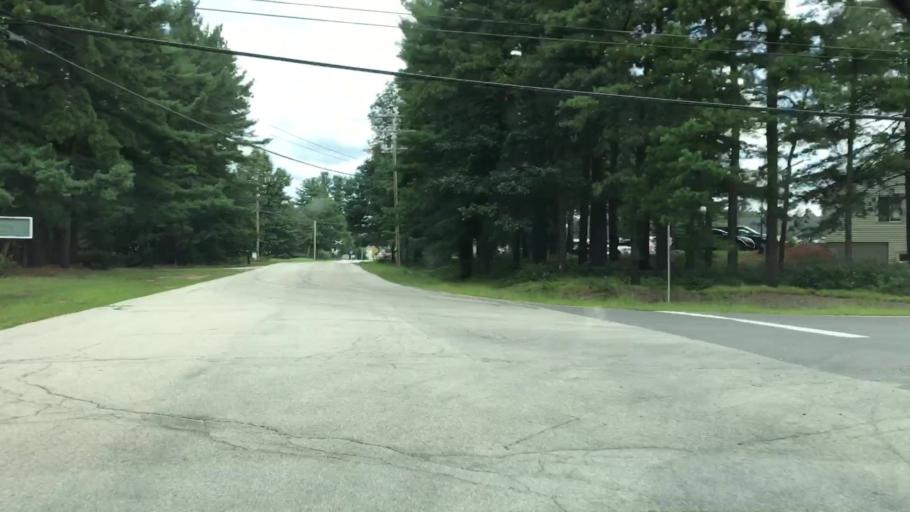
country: US
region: New Hampshire
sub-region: Hillsborough County
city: Hollis
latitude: 42.8075
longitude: -71.5827
